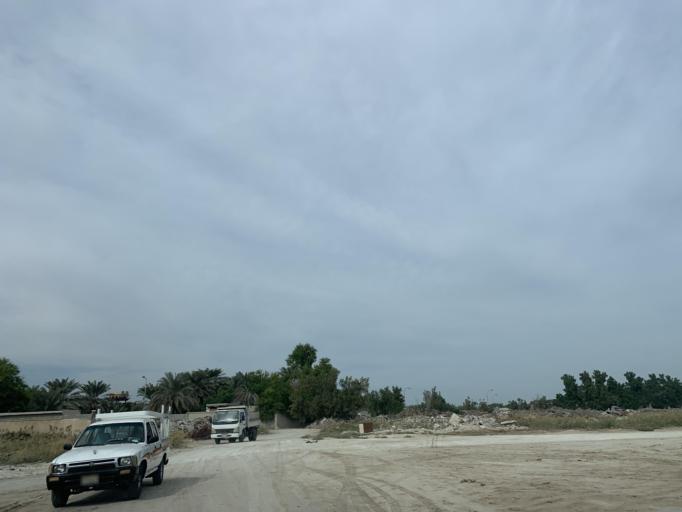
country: BH
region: Central Governorate
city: Madinat Hamad
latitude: 26.1099
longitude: 50.4718
